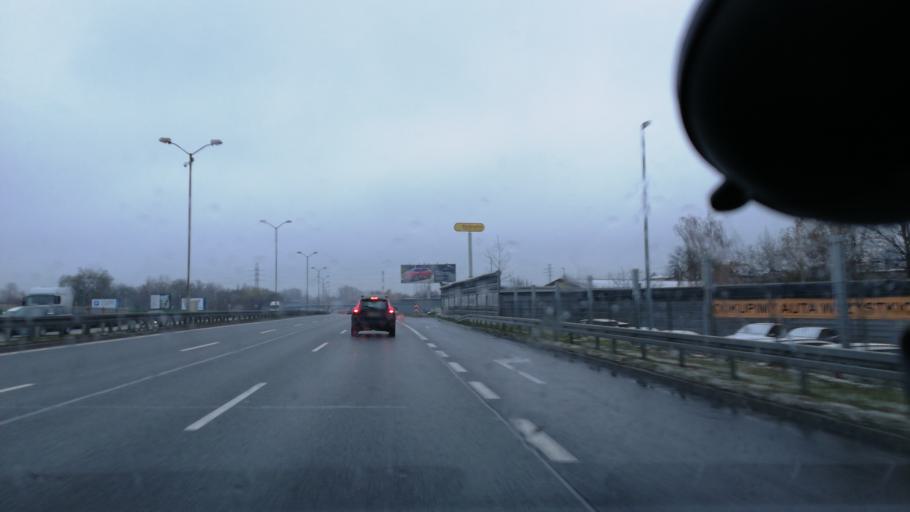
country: PL
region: Silesian Voivodeship
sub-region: Chorzow
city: Chorzow
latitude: 50.2781
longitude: 18.9553
